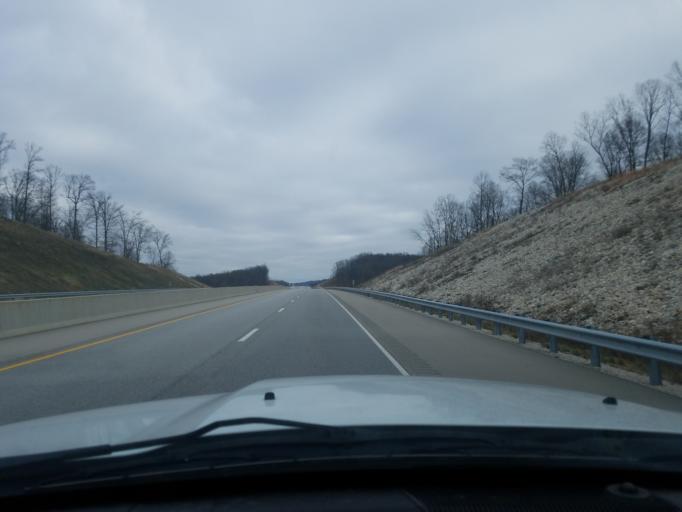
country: US
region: Indiana
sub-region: Greene County
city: Bloomfield
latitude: 38.9620
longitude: -86.8171
